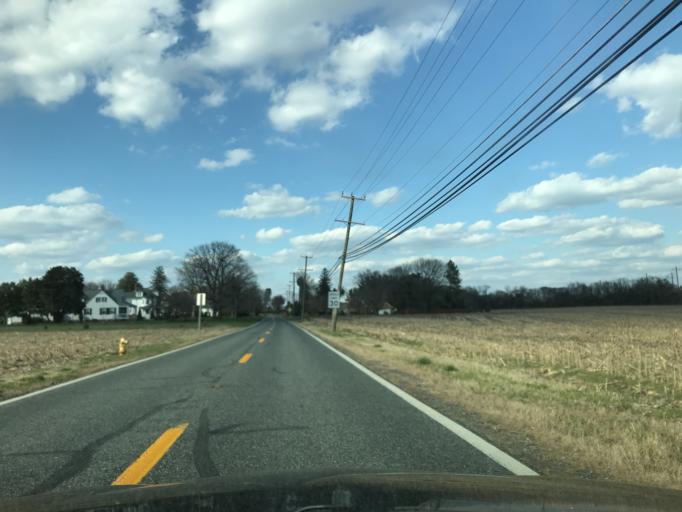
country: US
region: Maryland
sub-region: Harford County
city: Perryman
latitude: 39.4615
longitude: -76.2073
